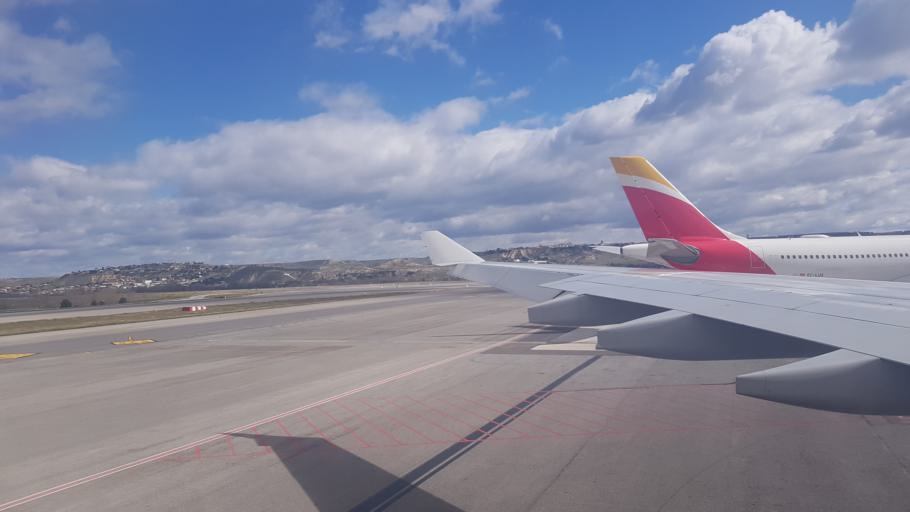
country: ES
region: Madrid
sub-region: Provincia de Madrid
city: Barajas de Madrid
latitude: 40.4997
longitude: -3.5690
